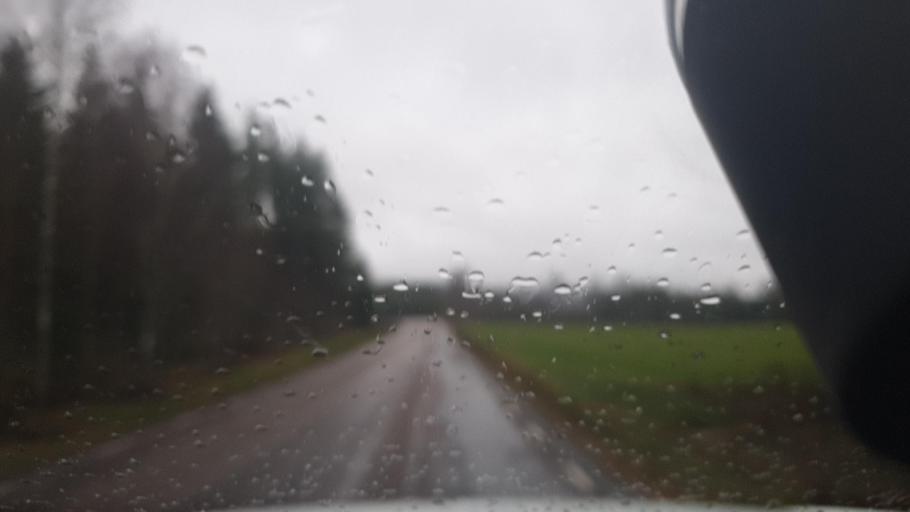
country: SE
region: Vaermland
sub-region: Eda Kommun
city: Amotfors
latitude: 59.7338
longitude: 12.1698
